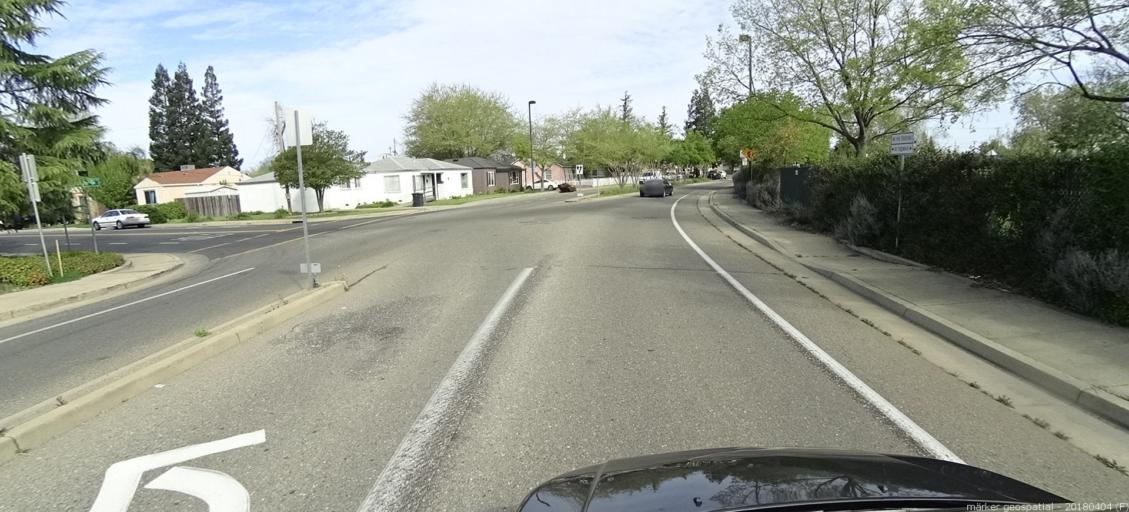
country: US
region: California
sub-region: Sacramento County
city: Galt
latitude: 38.2498
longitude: -121.3005
